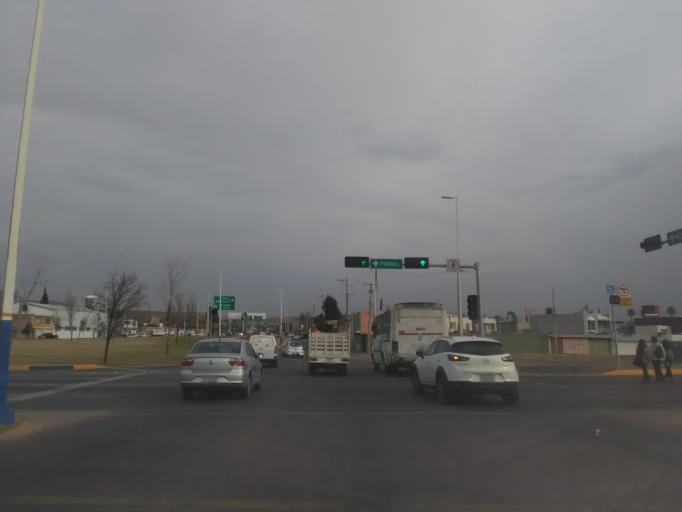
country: MX
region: Durango
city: Victoria de Durango
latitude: 24.0375
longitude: -104.6575
